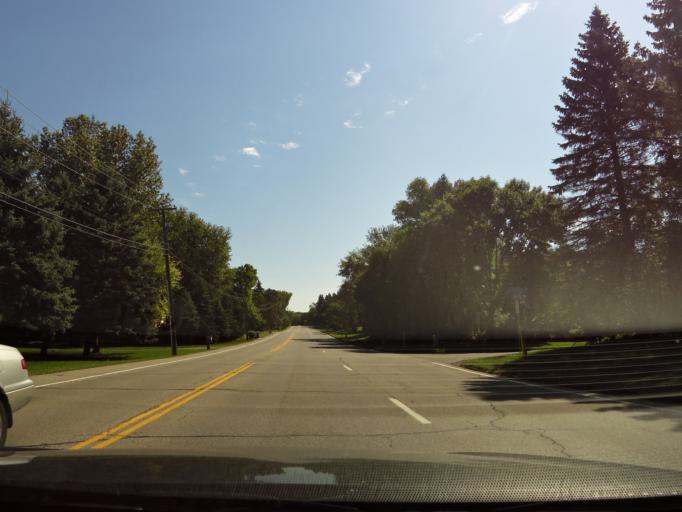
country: US
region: Minnesota
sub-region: Hennepin County
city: Hopkins
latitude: 44.9389
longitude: -93.4789
